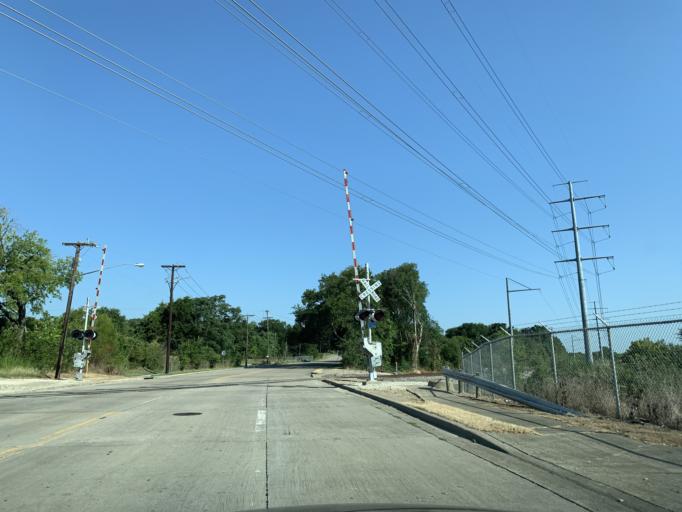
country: US
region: Texas
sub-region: Dallas County
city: Hutchins
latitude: 32.6631
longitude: -96.7412
